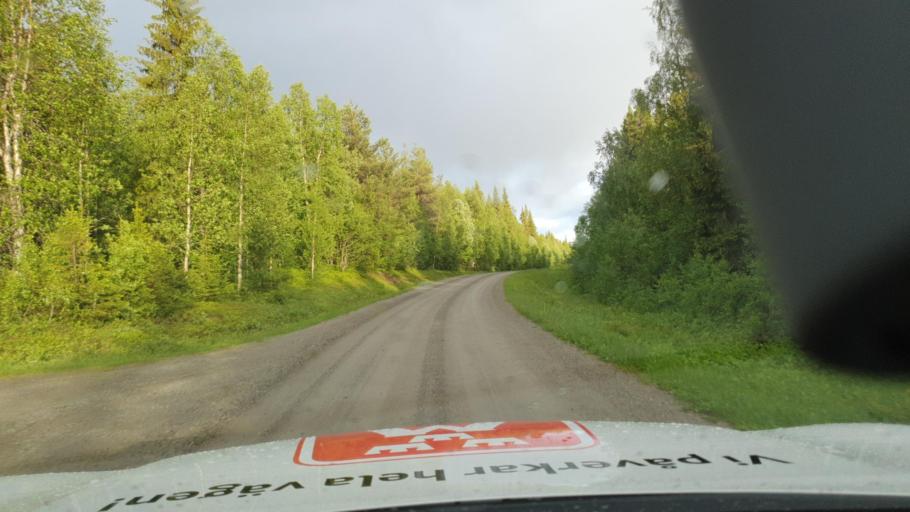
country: SE
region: Vaesterbotten
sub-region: Storumans Kommun
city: Storuman
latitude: 64.7858
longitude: 17.0263
